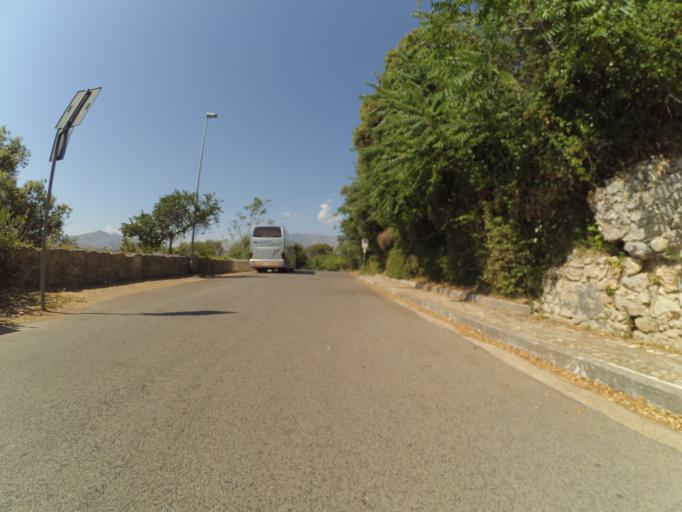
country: IT
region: Latium
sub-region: Provincia di Latina
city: Gaeta
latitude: 41.2087
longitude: 13.5727
